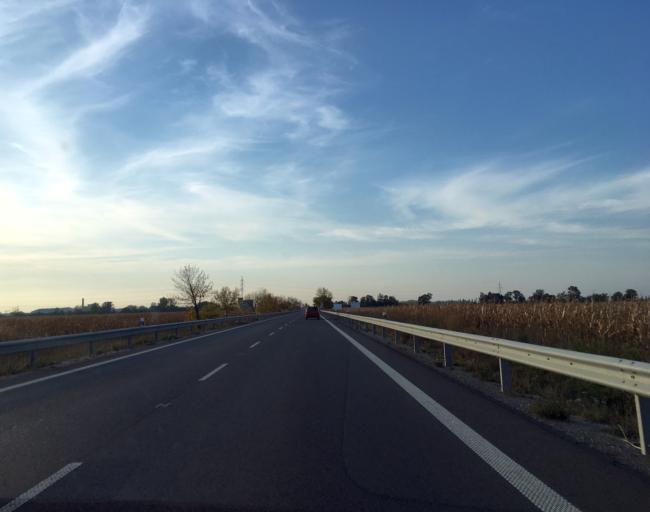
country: SK
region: Trnavsky
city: Sladkovicovo
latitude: 48.2022
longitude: 17.6674
